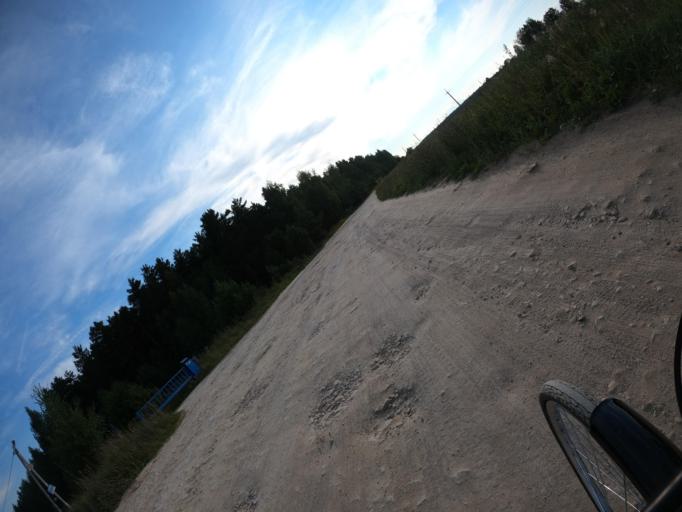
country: RU
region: Moskovskaya
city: Meshcherino
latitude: 55.1405
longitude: 38.4292
